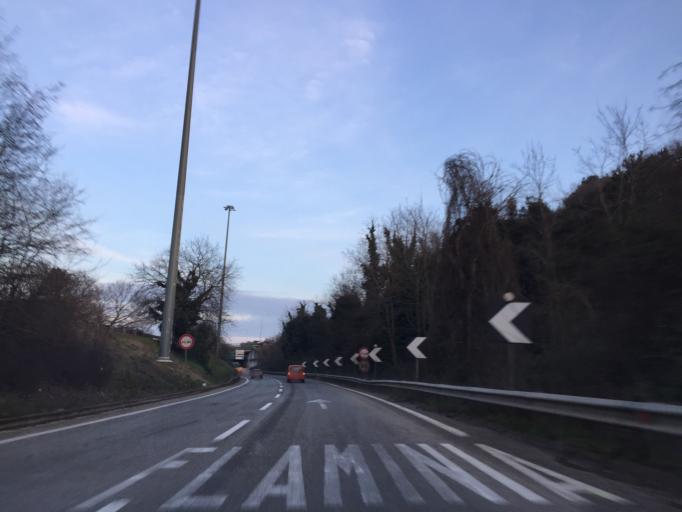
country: IT
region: Latium
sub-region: Citta metropolitana di Roma Capitale
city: Monte Caminetto
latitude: 41.9876
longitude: 12.4717
